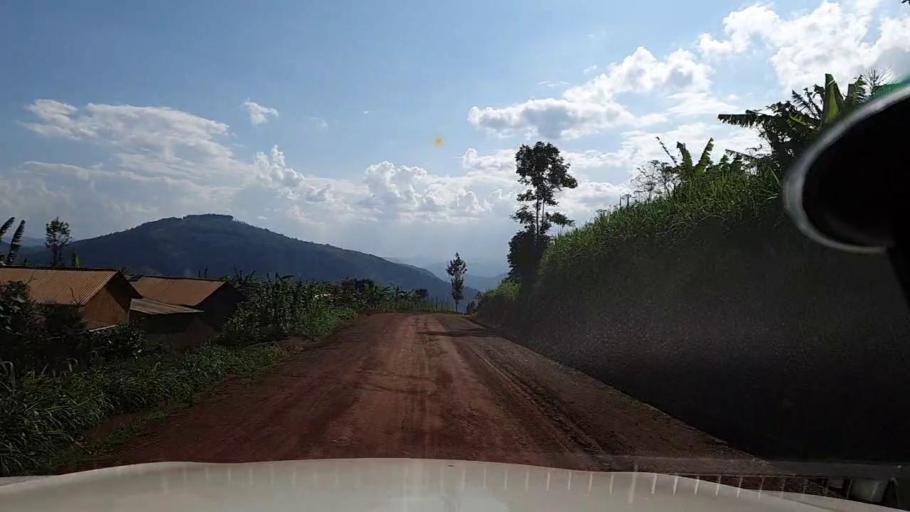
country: RW
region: Kigali
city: Kigali
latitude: -1.8392
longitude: 29.8512
